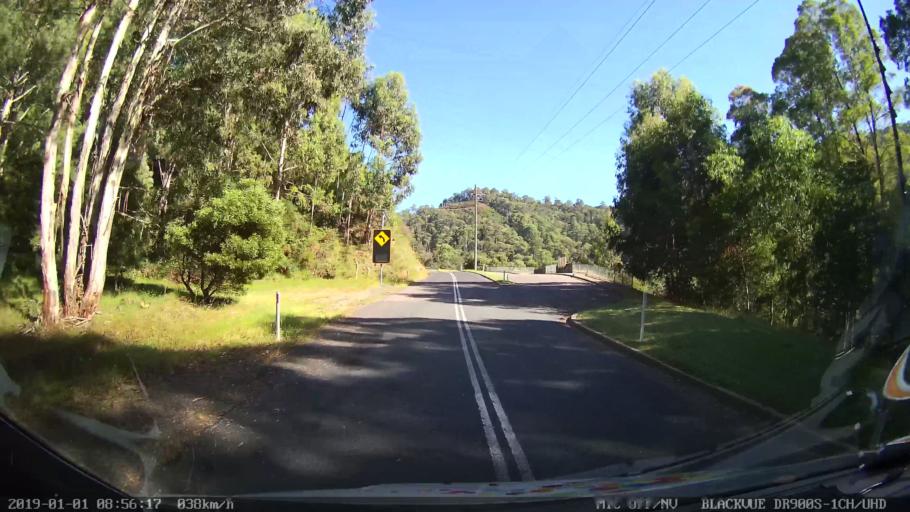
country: AU
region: New South Wales
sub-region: Snowy River
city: Jindabyne
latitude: -36.2478
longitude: 148.1888
